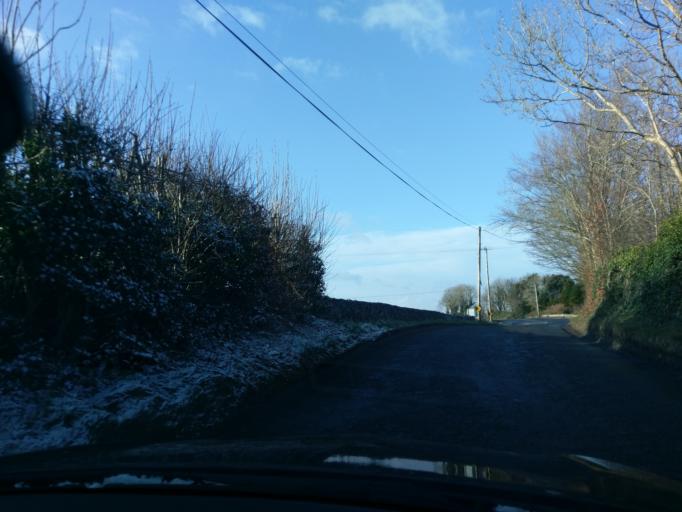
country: IE
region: Connaught
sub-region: County Galway
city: Gort
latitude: 53.1636
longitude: -8.7833
